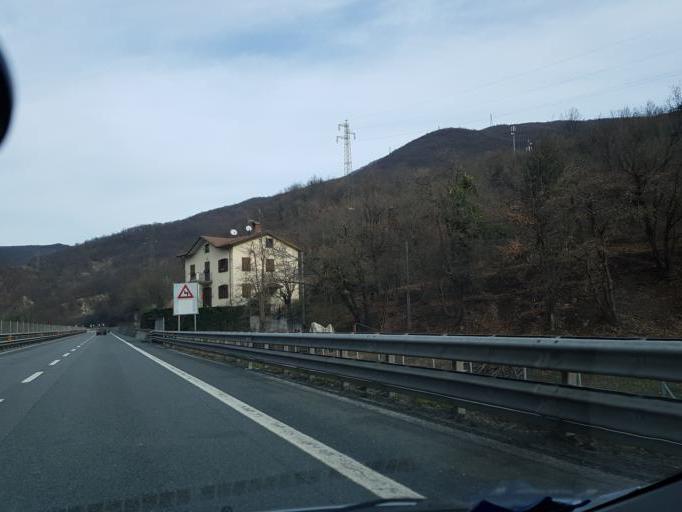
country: IT
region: Liguria
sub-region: Provincia di Genova
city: Isola del Cantone
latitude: 44.6473
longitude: 8.9594
